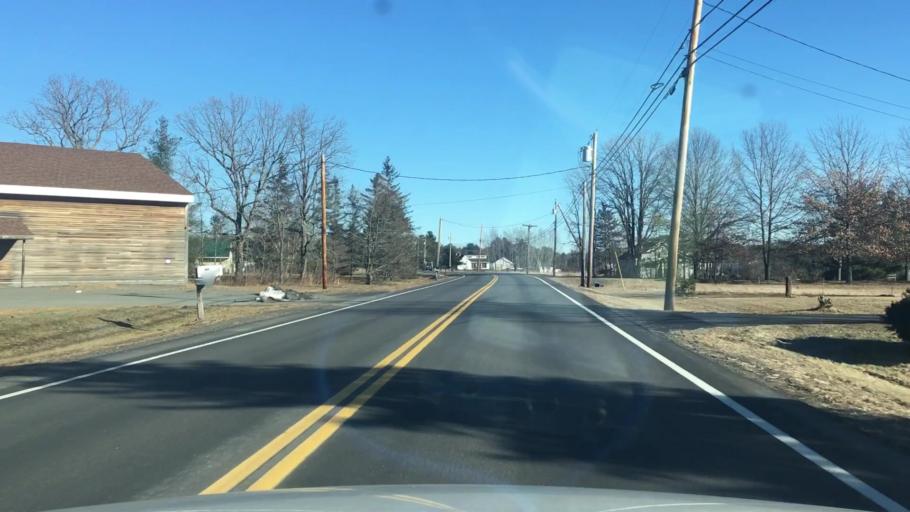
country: US
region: Maine
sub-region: Kennebec County
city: Benton
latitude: 44.6041
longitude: -69.5365
